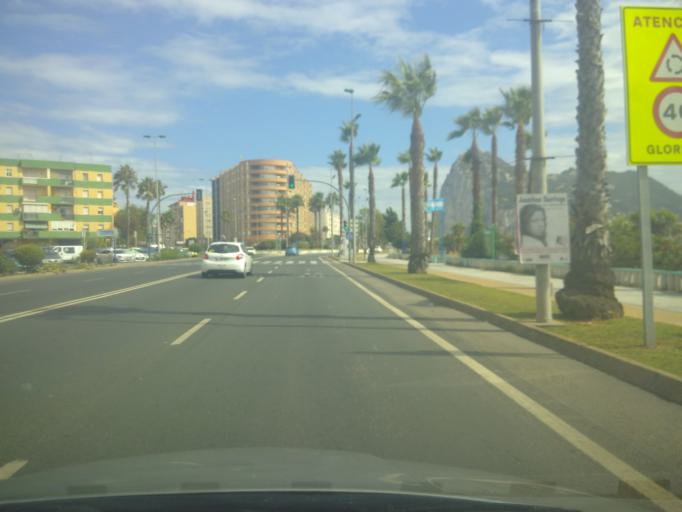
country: ES
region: Andalusia
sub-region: Provincia de Cadiz
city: La Linea de la Concepcion
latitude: 36.1633
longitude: -5.3584
